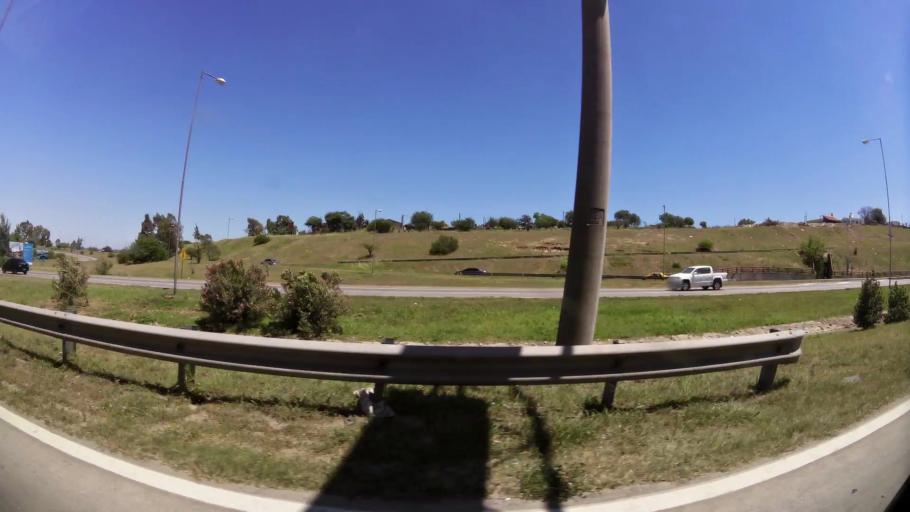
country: AR
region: Cordoba
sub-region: Departamento de Capital
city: Cordoba
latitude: -31.3953
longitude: -64.1275
